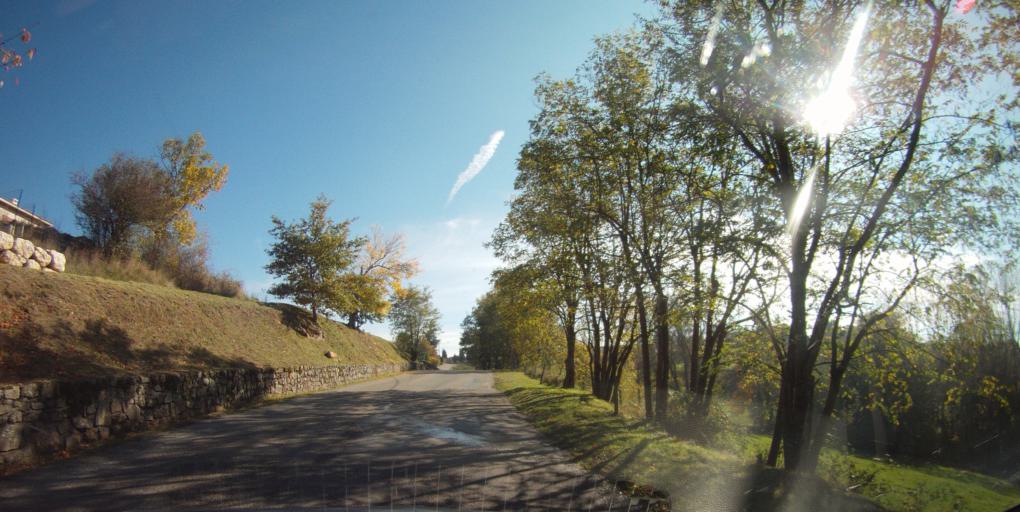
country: FR
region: Rhone-Alpes
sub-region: Departement de l'Ardeche
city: Vernoux-en-Vivarais
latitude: 44.8980
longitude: 4.6386
